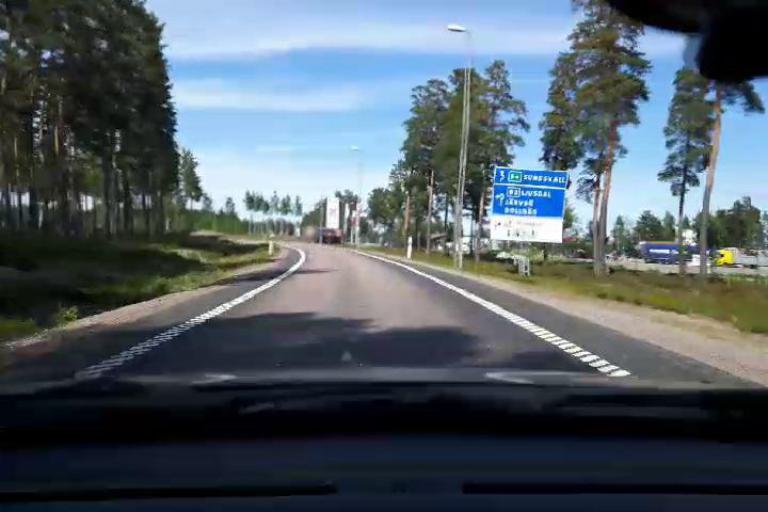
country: SE
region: Gaevleborg
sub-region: Gavle Kommun
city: Norrsundet
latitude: 61.0705
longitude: 16.9655
